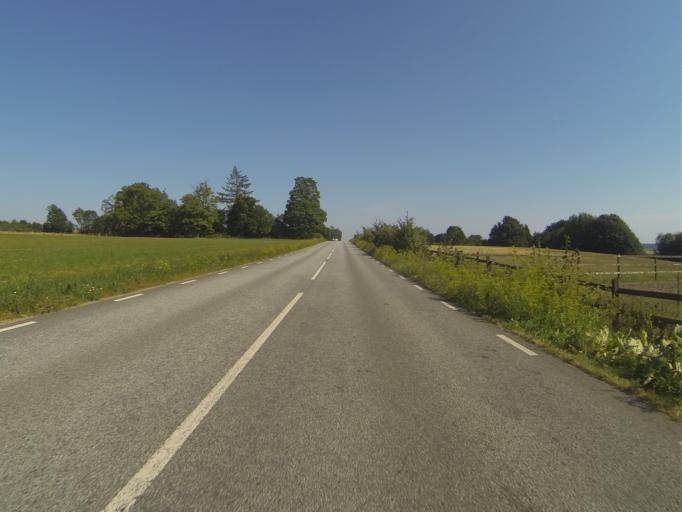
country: SE
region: Skane
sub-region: Hoors Kommun
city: Loberod
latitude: 55.7126
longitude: 13.5401
